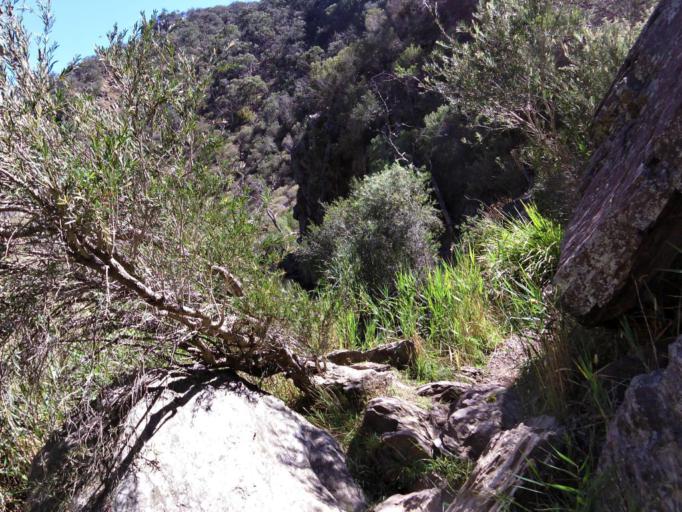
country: AU
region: Victoria
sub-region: Moorabool
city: Bacchus Marsh
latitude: -37.6646
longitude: 144.3539
